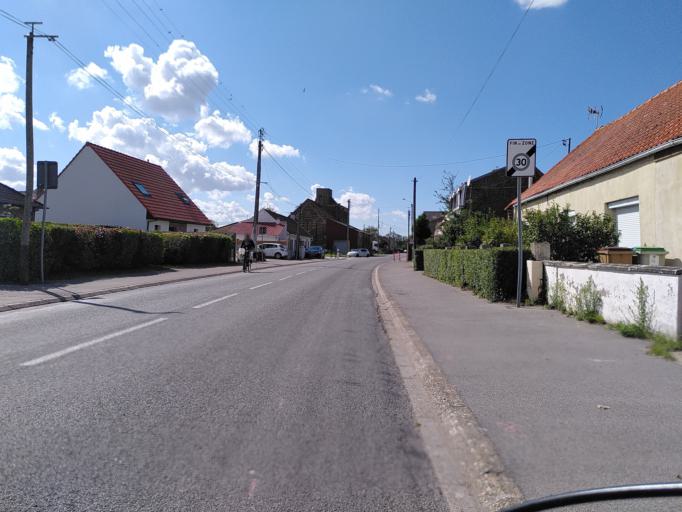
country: FR
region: Nord-Pas-de-Calais
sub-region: Departement du Nord
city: Grand-Fort-Philippe
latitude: 50.9886
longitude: 2.0845
